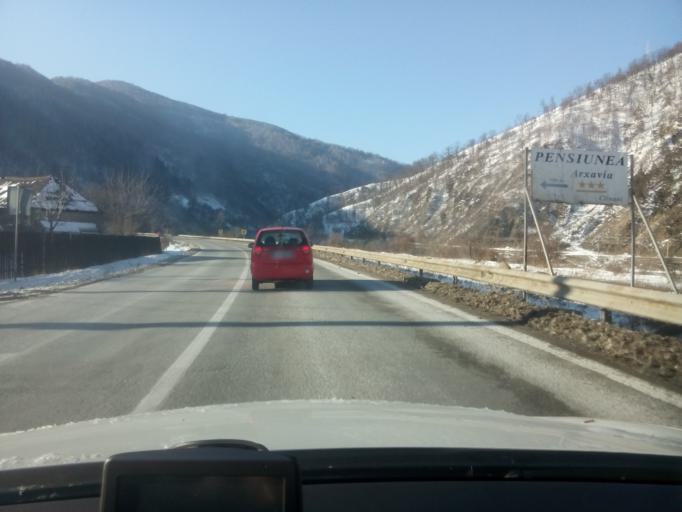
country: RO
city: Cainenii Mici
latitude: 45.5000
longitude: 24.2997
